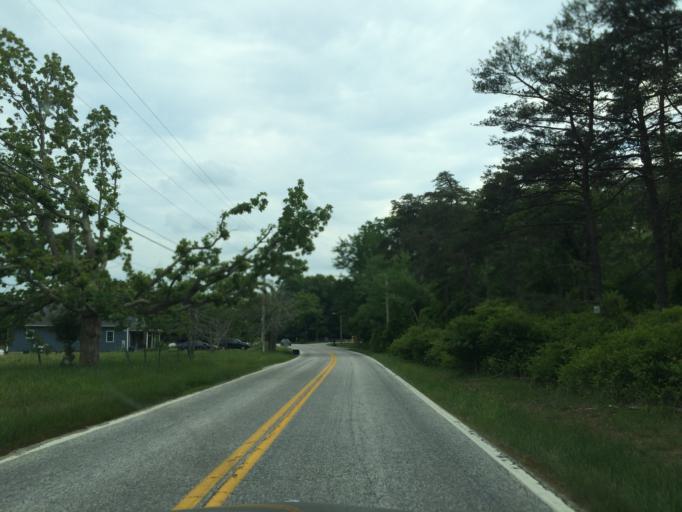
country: US
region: Maryland
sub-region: Baltimore County
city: Owings Mills
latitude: 39.4114
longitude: -76.8357
